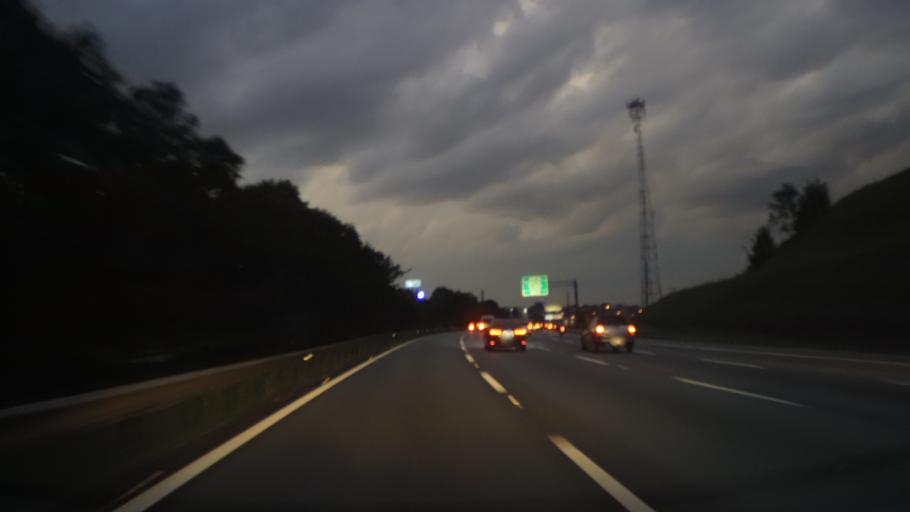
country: BR
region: Sao Paulo
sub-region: Diadema
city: Diadema
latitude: -23.7285
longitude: -46.6066
